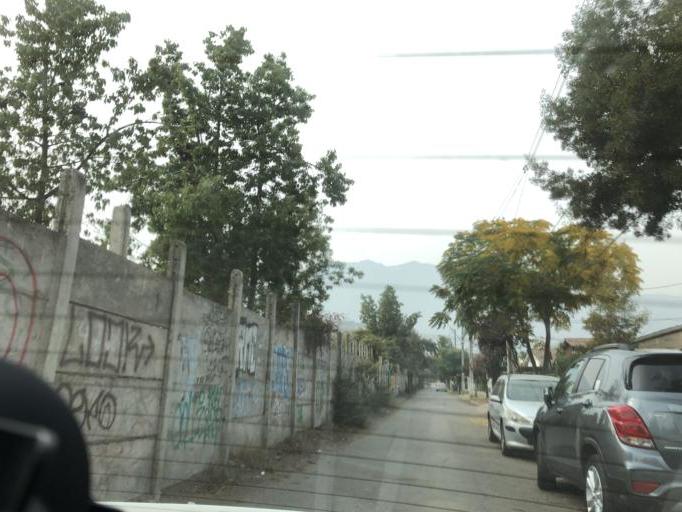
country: CL
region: Santiago Metropolitan
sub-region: Provincia de Cordillera
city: Puente Alto
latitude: -33.5555
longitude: -70.5562
